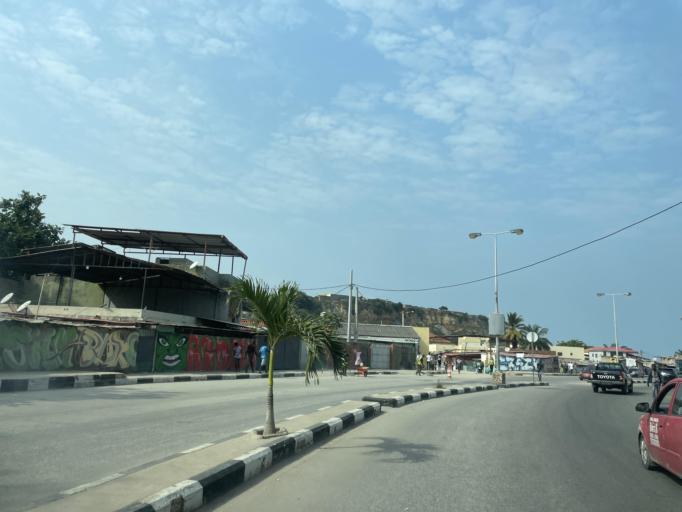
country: AO
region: Luanda
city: Luanda
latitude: -8.8299
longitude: 13.2166
